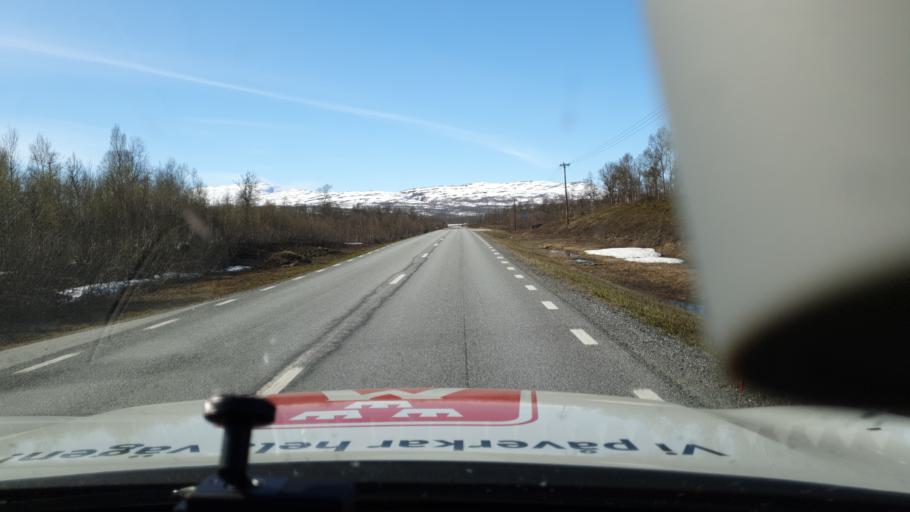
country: NO
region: Nordland
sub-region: Rana
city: Mo i Rana
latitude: 66.0296
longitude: 15.0782
